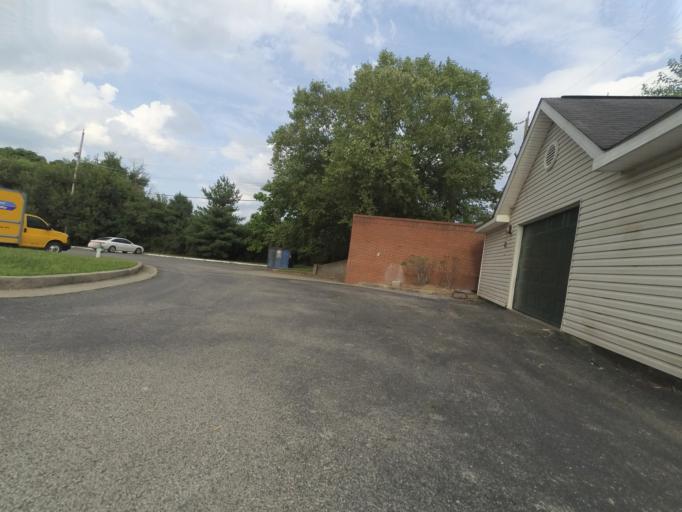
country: US
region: West Virginia
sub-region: Cabell County
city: Huntington
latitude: 38.4205
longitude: -82.4184
